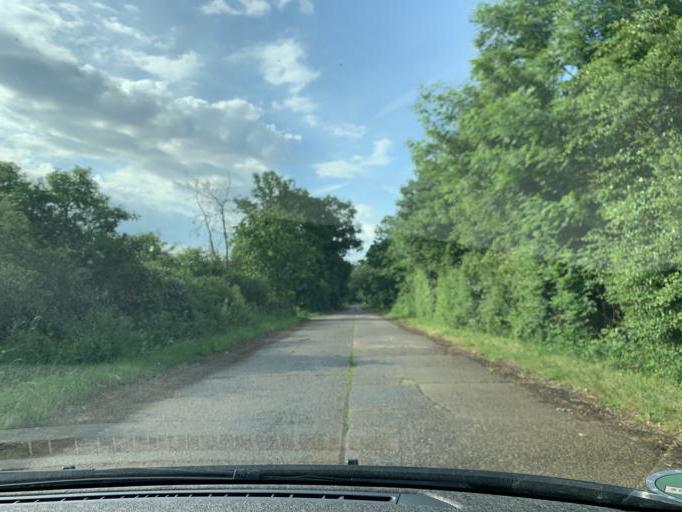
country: DE
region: North Rhine-Westphalia
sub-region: Regierungsbezirk Koln
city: Kreuzau
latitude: 50.7562
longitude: 6.5191
